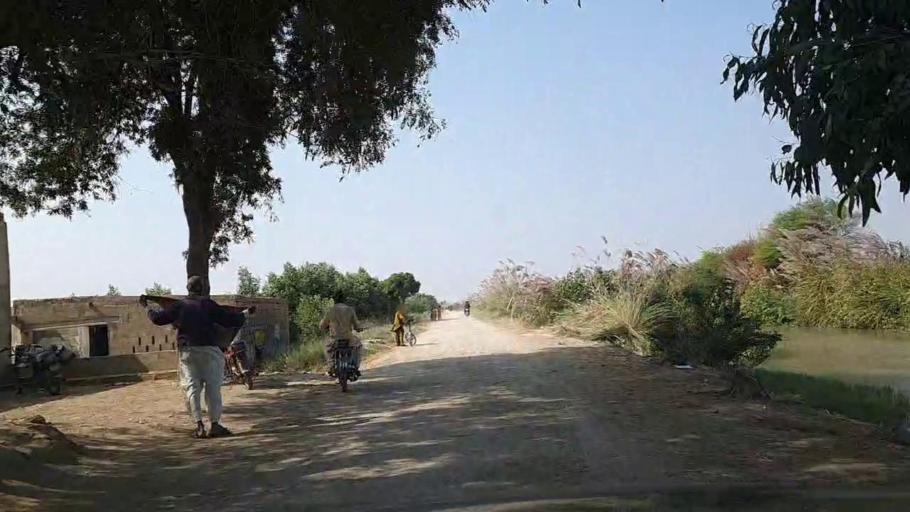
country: PK
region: Sindh
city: Gharo
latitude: 24.7029
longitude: 67.6386
